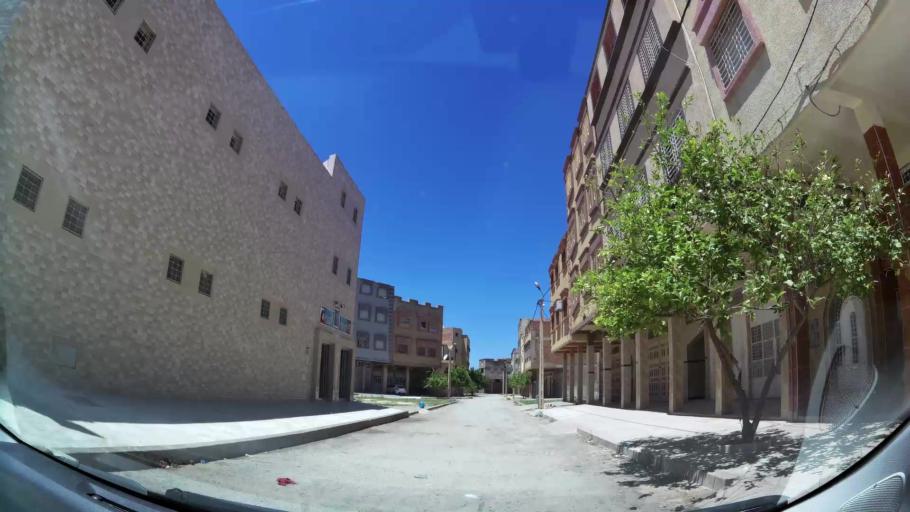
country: MA
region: Oriental
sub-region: Oujda-Angad
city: Oujda
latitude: 34.6771
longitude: -1.8718
